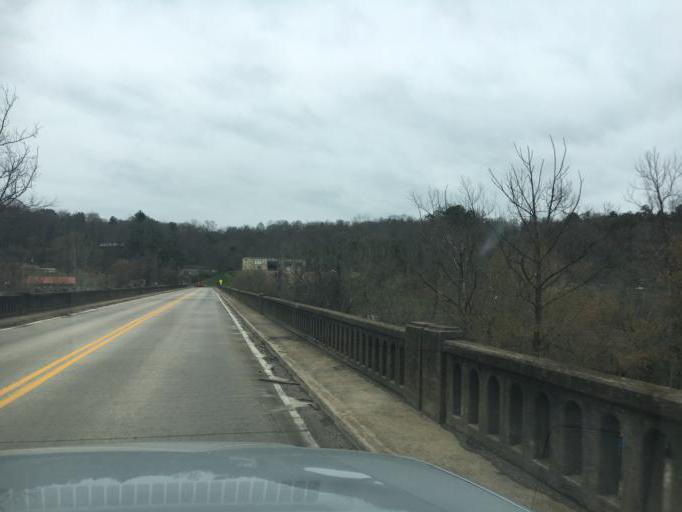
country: US
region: North Carolina
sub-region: Buncombe County
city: Woodfin
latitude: 35.6284
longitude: -82.6010
